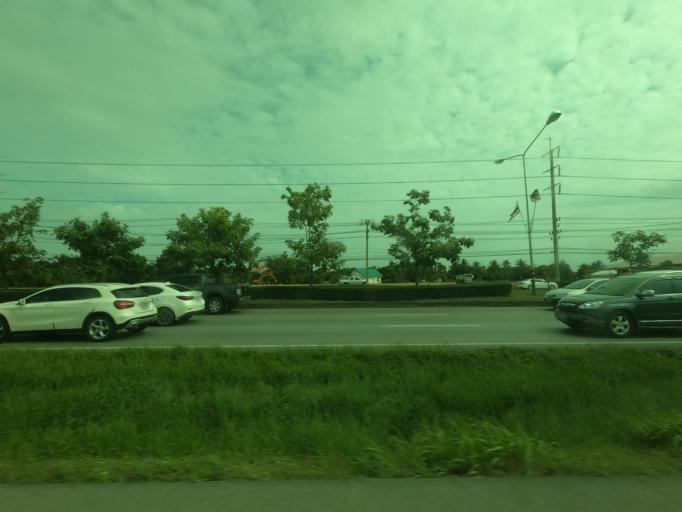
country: TH
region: Nakhon Pathom
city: Nakhon Chai Si
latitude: 13.7699
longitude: 100.2024
